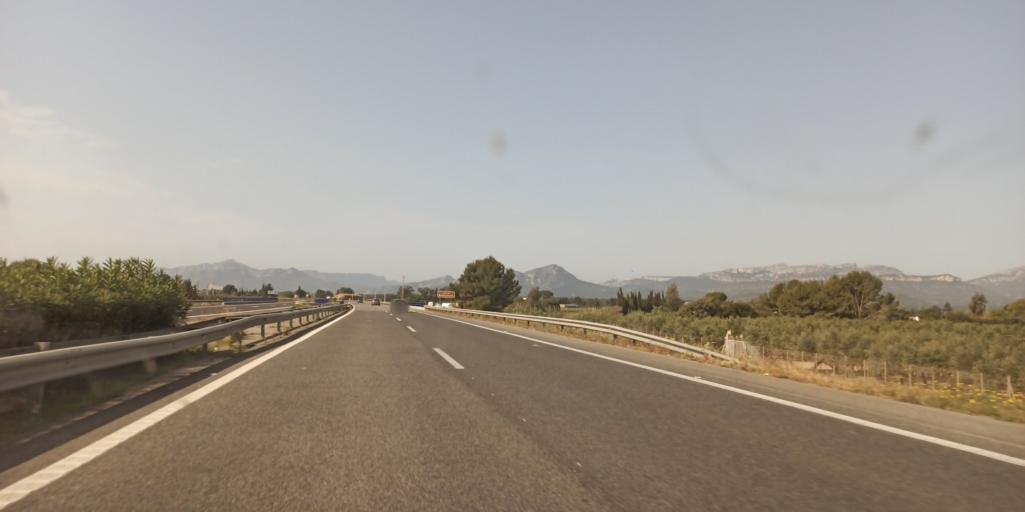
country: ES
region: Catalonia
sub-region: Provincia de Tarragona
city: Cambrils
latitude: 41.0693
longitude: 1.0061
